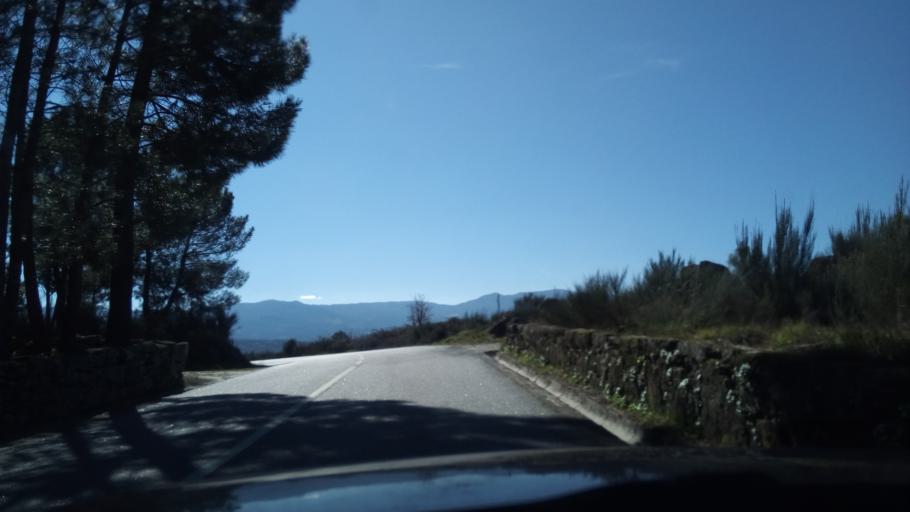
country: PT
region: Guarda
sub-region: Fornos de Algodres
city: Fornos de Algodres
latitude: 40.6017
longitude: -7.5144
